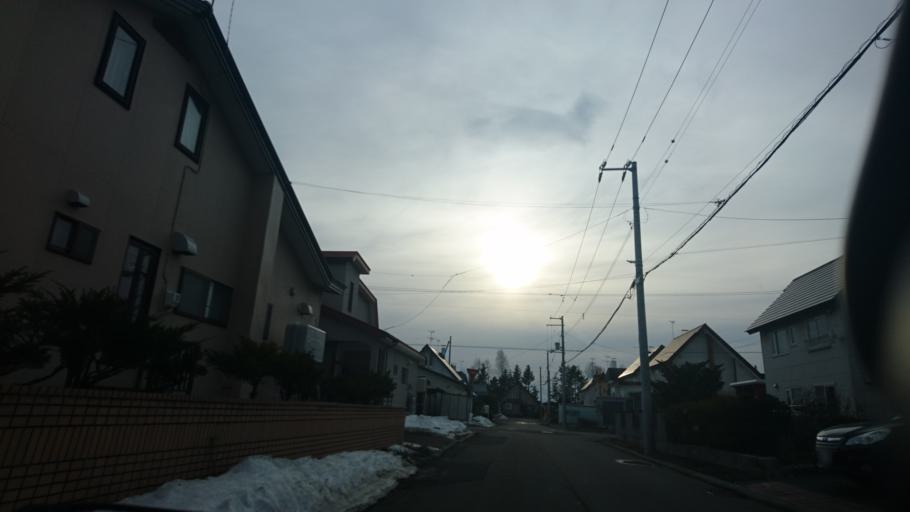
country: JP
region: Hokkaido
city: Otofuke
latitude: 42.9931
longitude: 143.1911
